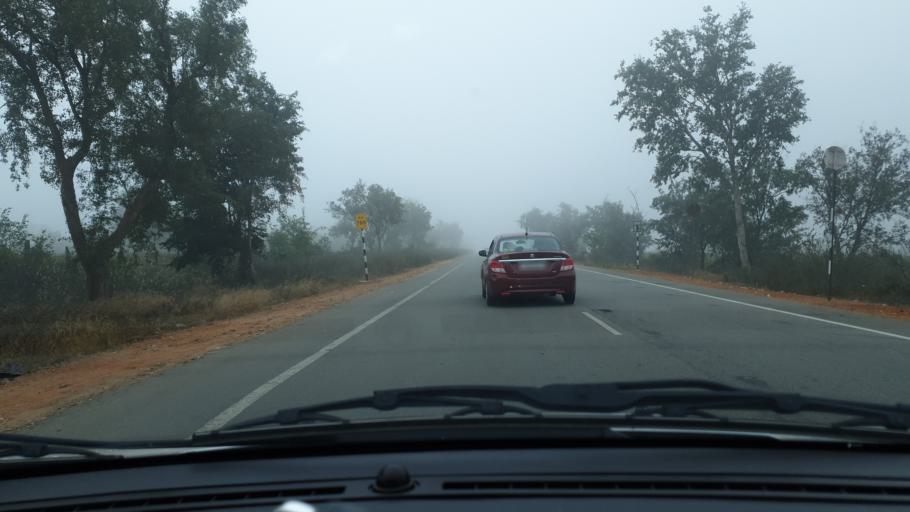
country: IN
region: Telangana
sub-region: Mahbubnagar
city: Nagar Karnul
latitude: 16.6593
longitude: 78.5766
